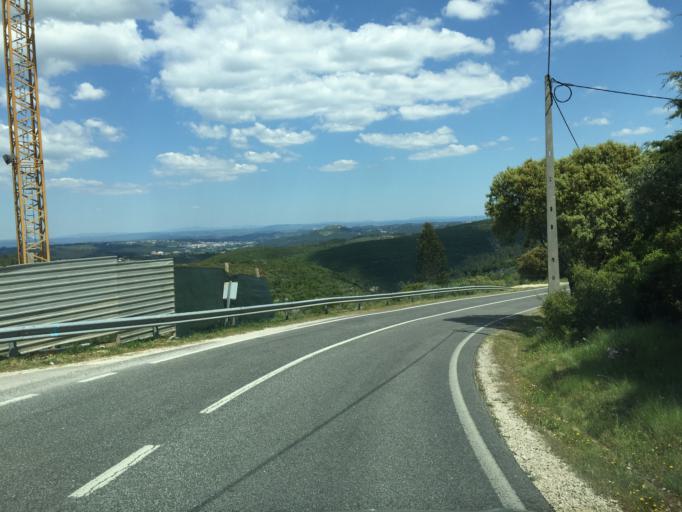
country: PT
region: Santarem
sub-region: Ourem
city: Fatima
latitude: 39.6341
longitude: -8.6630
